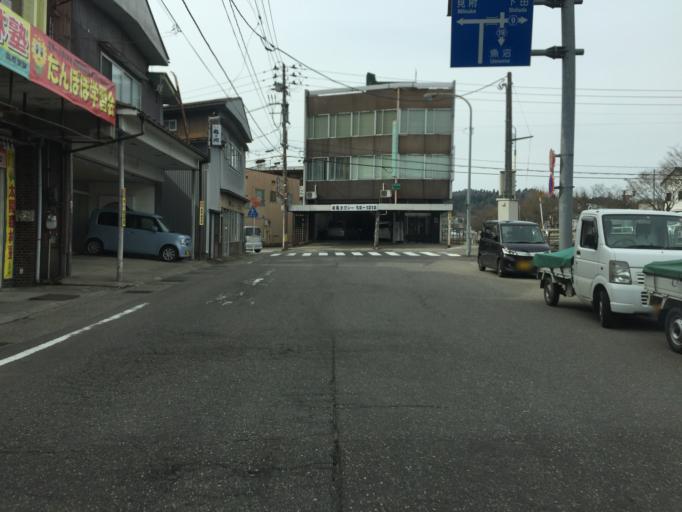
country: JP
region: Niigata
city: Tochio-honcho
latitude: 37.4755
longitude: 138.9937
